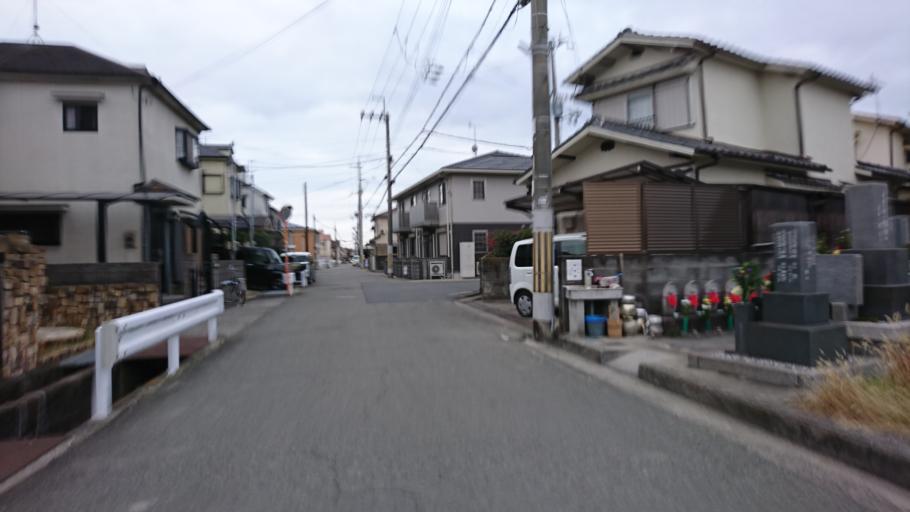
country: JP
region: Hyogo
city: Kakogawacho-honmachi
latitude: 34.7425
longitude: 134.8488
